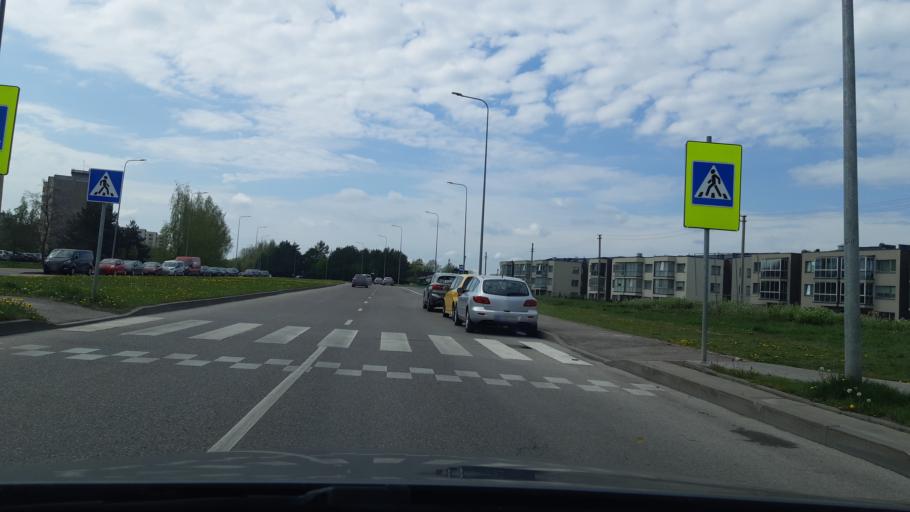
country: LT
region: Kauno apskritis
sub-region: Kaunas
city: Silainiai
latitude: 54.9219
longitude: 23.8683
